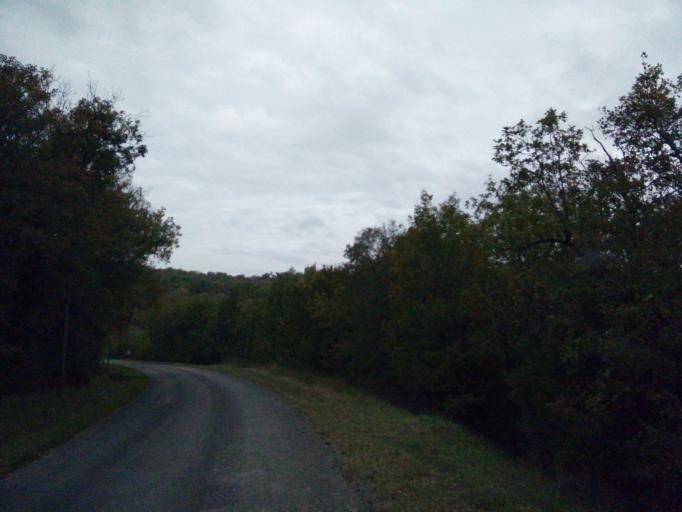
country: FR
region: Midi-Pyrenees
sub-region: Departement du Lot
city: Lalbenque
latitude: 44.5103
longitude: 1.6449
